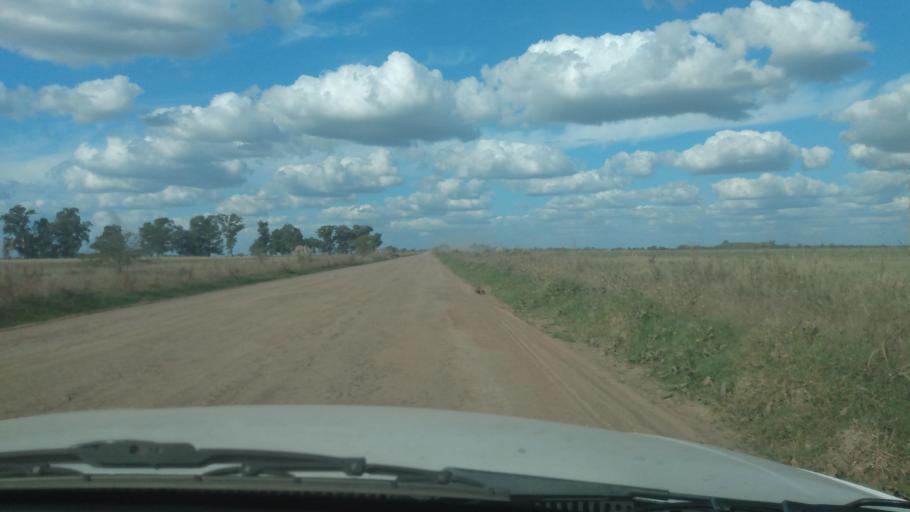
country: AR
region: Buenos Aires
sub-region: Partido de Navarro
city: Navarro
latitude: -35.0122
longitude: -59.4445
